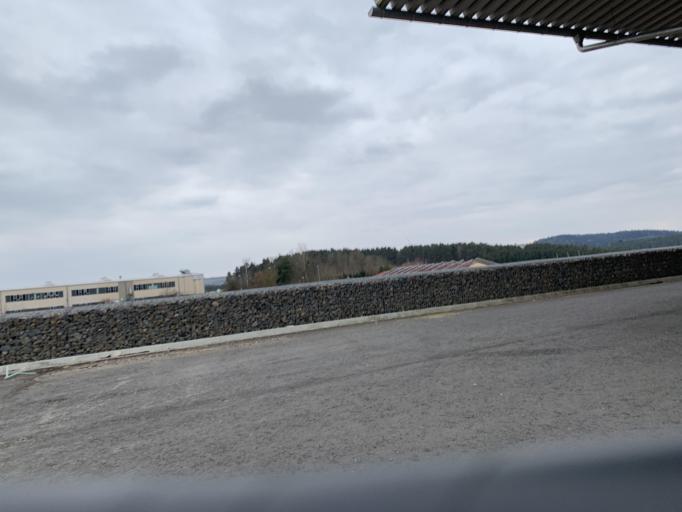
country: DE
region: Bavaria
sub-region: Upper Palatinate
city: Neunburg vorm Wald
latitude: 49.3363
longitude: 12.3973
